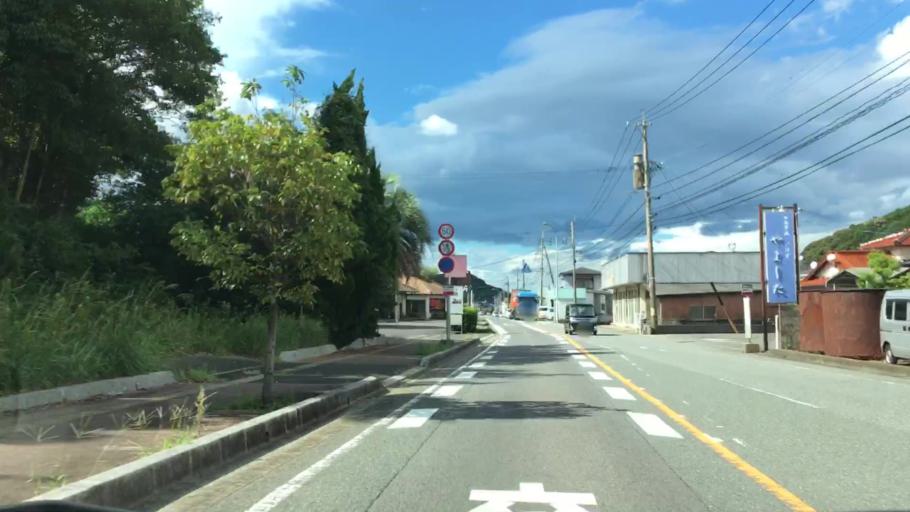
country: JP
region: Saga Prefecture
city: Imaricho-ko
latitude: 33.1884
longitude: 129.8522
